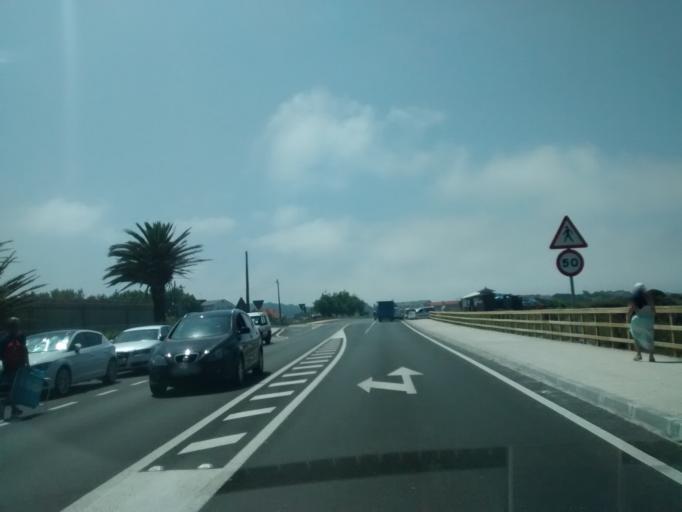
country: ES
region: Galicia
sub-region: Provincia de Pontevedra
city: O Grove
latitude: 42.4380
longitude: -8.8709
